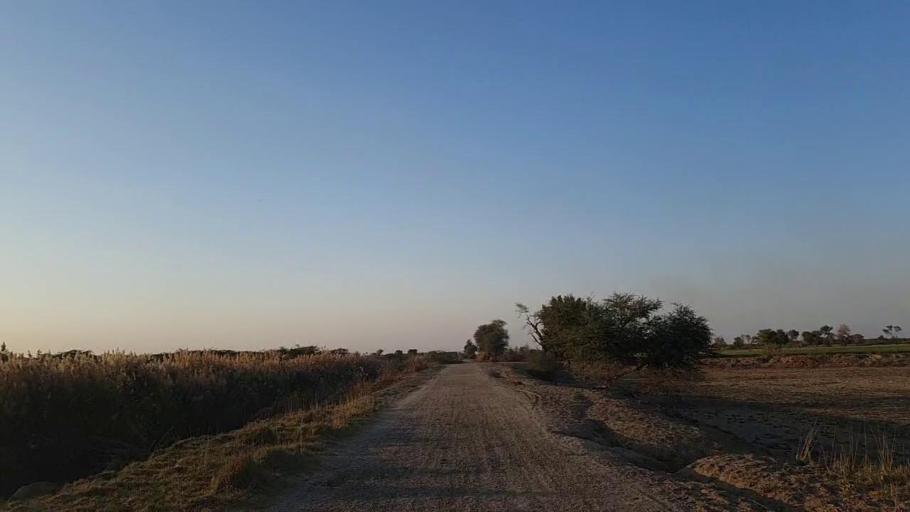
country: PK
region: Sindh
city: Jam Sahib
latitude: 26.3389
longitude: 68.6186
